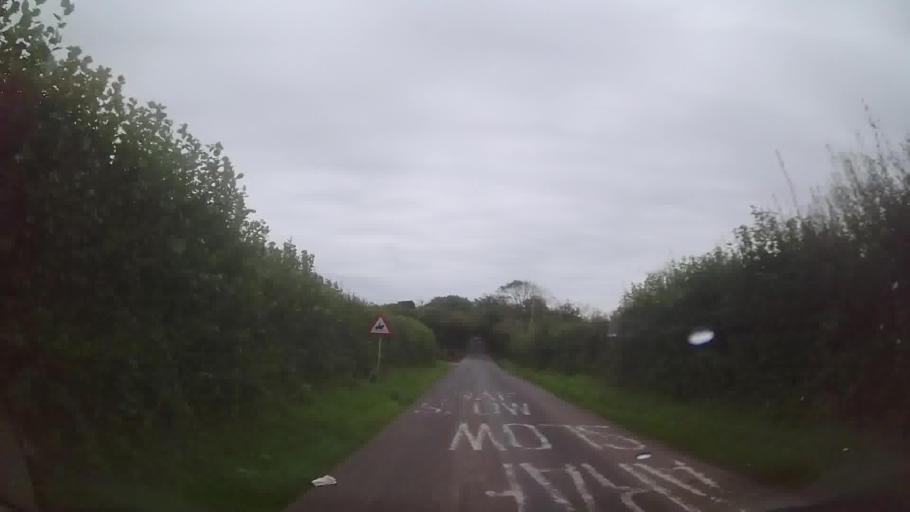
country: GB
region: Wales
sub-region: Carmarthenshire
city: Whitland
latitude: 51.7497
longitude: -4.6091
